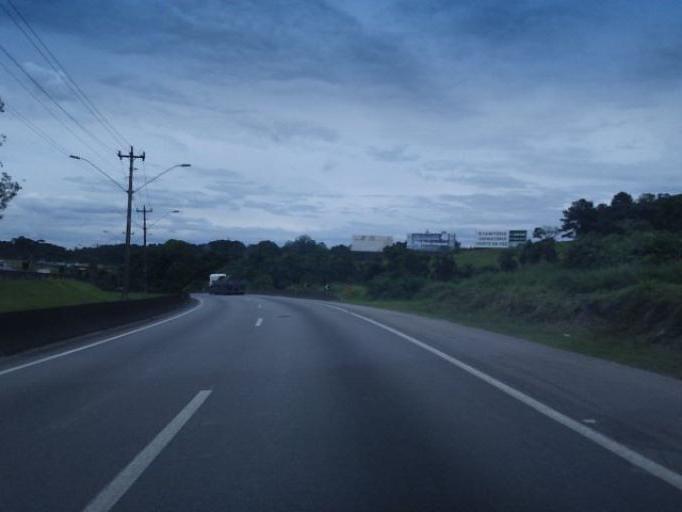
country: BR
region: Sao Paulo
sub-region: Itapecerica Da Serra
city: Itapecerica da Serra
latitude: -23.7235
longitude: -46.8922
